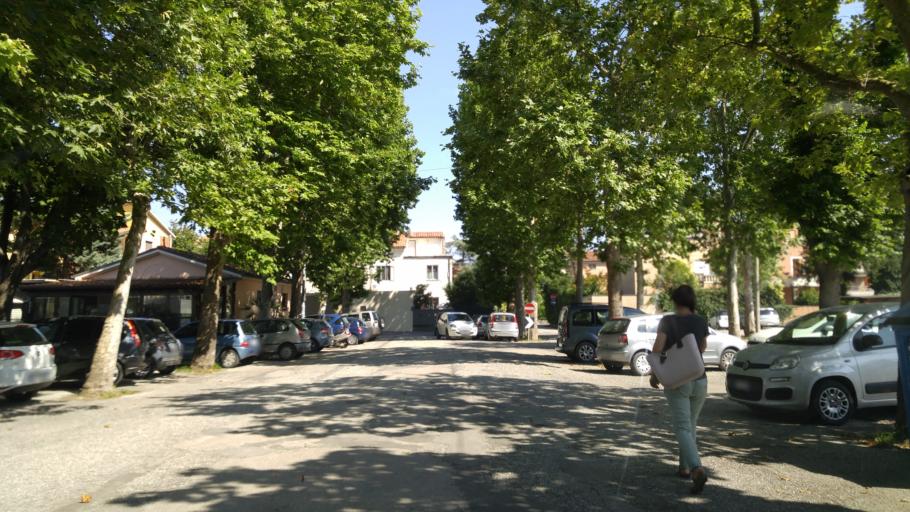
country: IT
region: The Marches
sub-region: Provincia di Pesaro e Urbino
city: Fano
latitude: 43.8373
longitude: 13.0205
